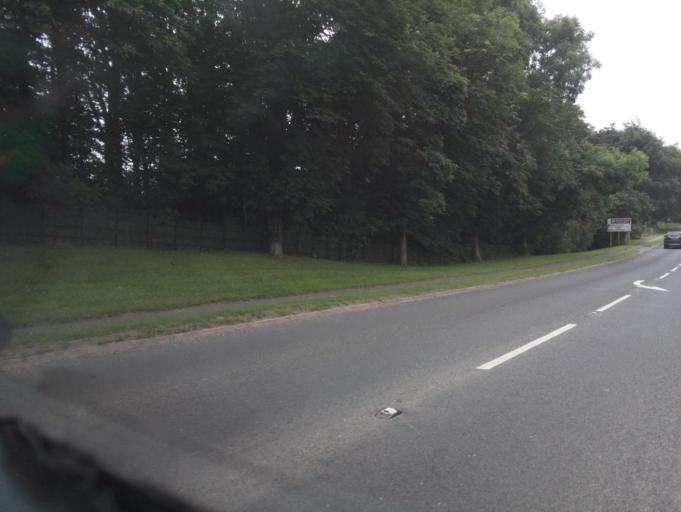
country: GB
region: England
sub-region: District of Rutland
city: Empingham
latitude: 52.6644
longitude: -0.5956
